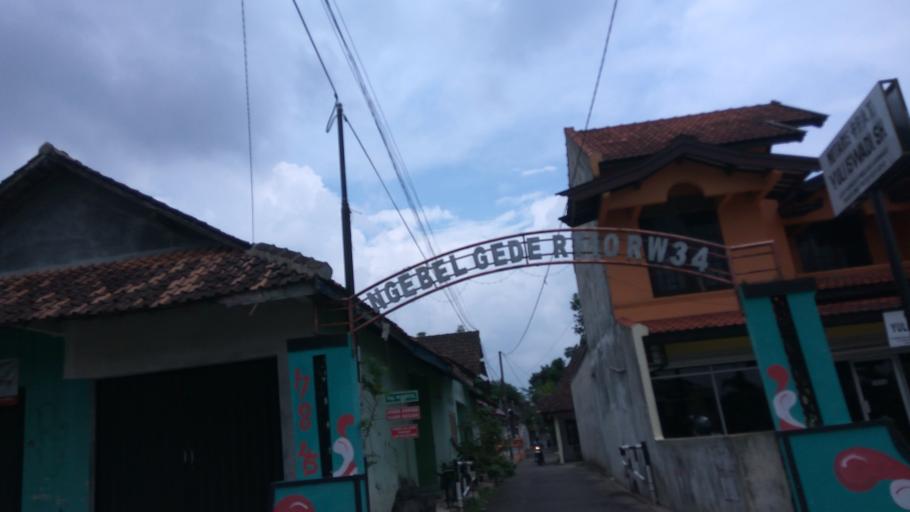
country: ID
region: Daerah Istimewa Yogyakarta
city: Melati
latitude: -7.7256
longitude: 110.3959
